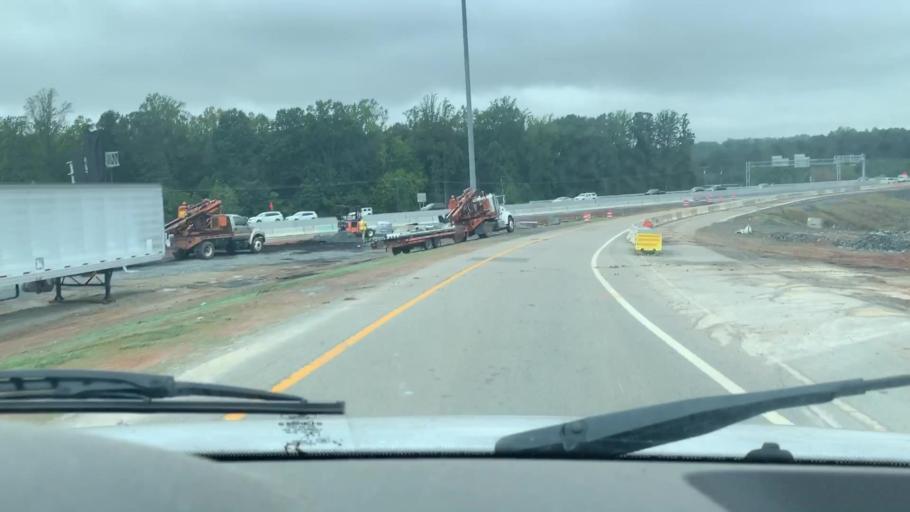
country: US
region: North Carolina
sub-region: Gaston County
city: Davidson
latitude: 35.5316
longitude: -80.8609
